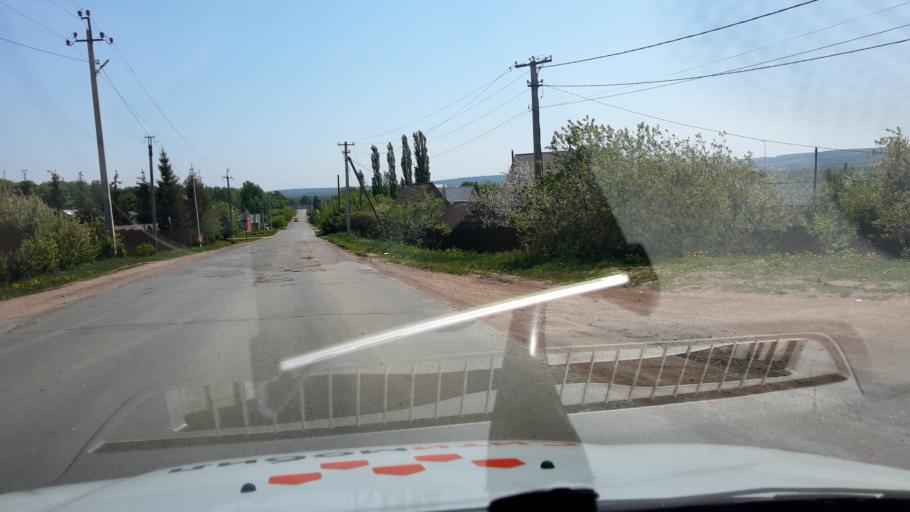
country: RU
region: Bashkortostan
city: Avdon
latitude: 54.6210
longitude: 55.6566
